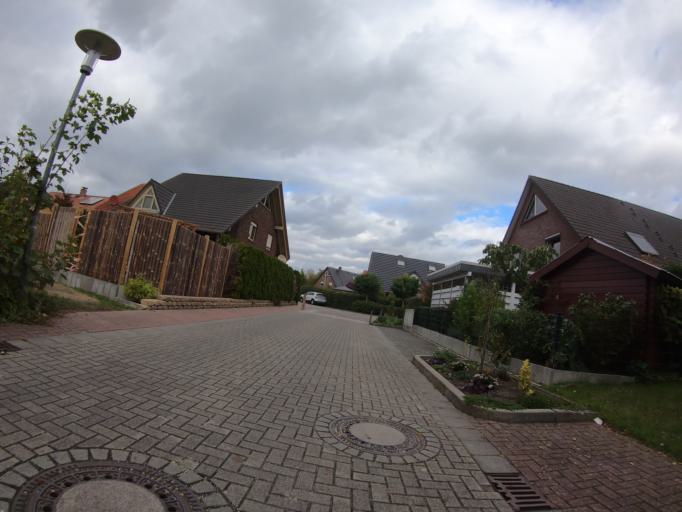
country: DE
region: Lower Saxony
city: Isenbuttel
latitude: 52.4386
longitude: 10.5780
